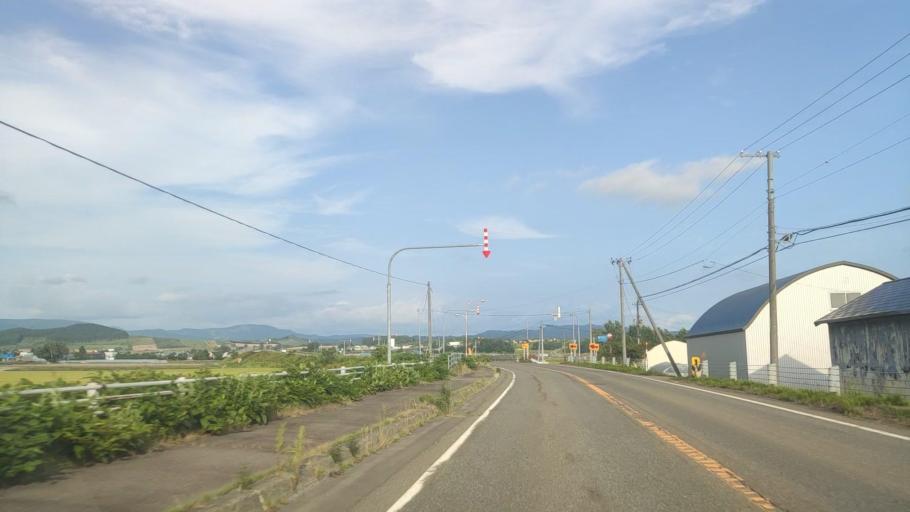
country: JP
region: Hokkaido
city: Iwamizawa
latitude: 43.0272
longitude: 141.8215
